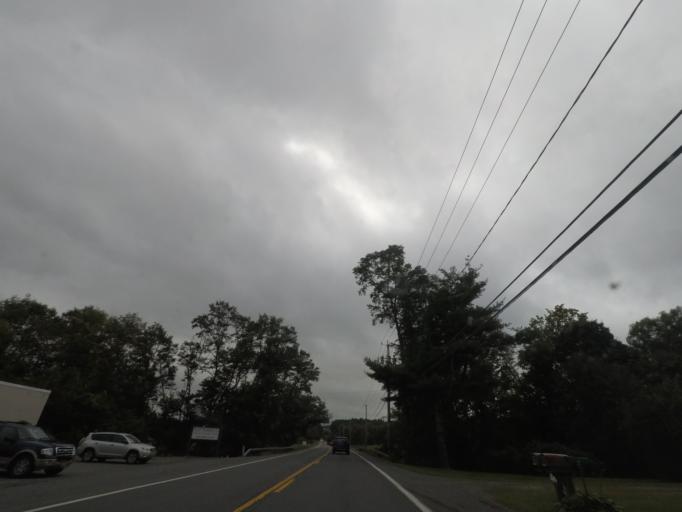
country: US
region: New York
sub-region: Rensselaer County
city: Hoosick Falls
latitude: 42.8870
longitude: -73.3600
